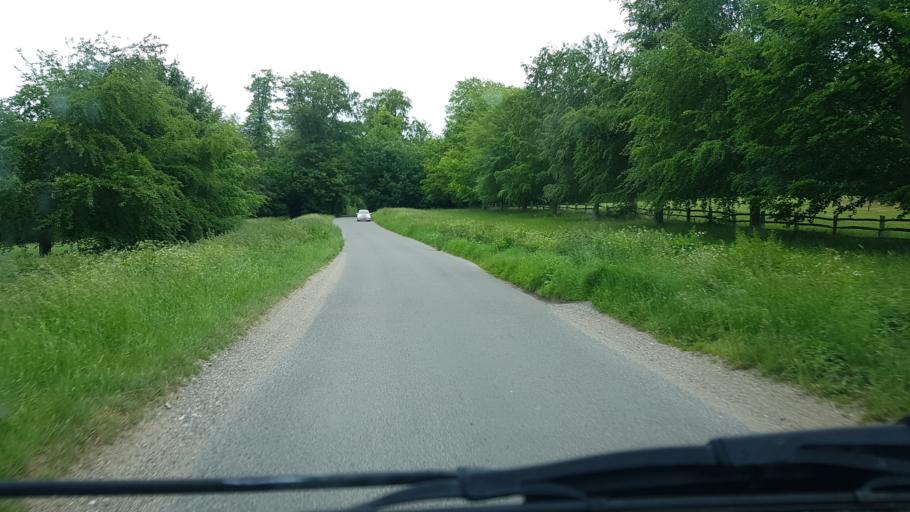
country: GB
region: England
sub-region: Surrey
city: Great Bookham
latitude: 51.2645
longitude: -0.3697
